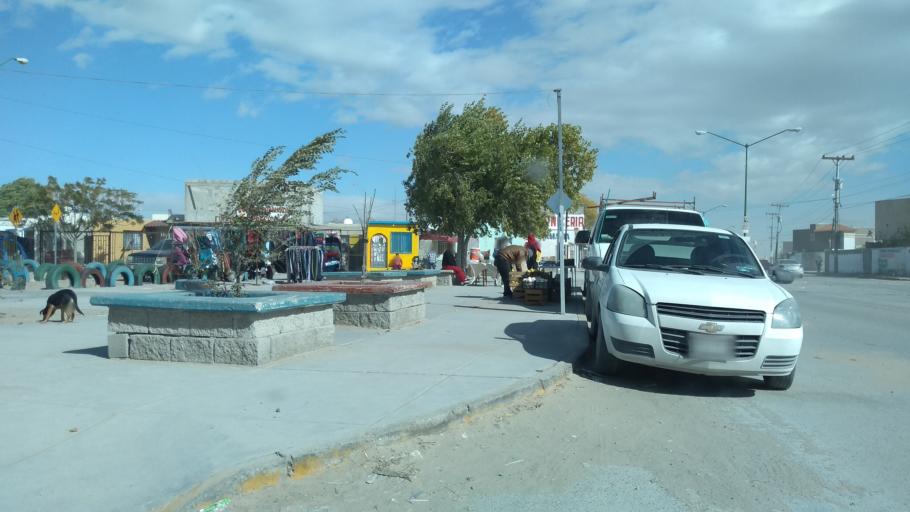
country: US
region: Texas
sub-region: El Paso County
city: Socorro Mission Number 1 Colonia
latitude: 31.5861
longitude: -106.3553
